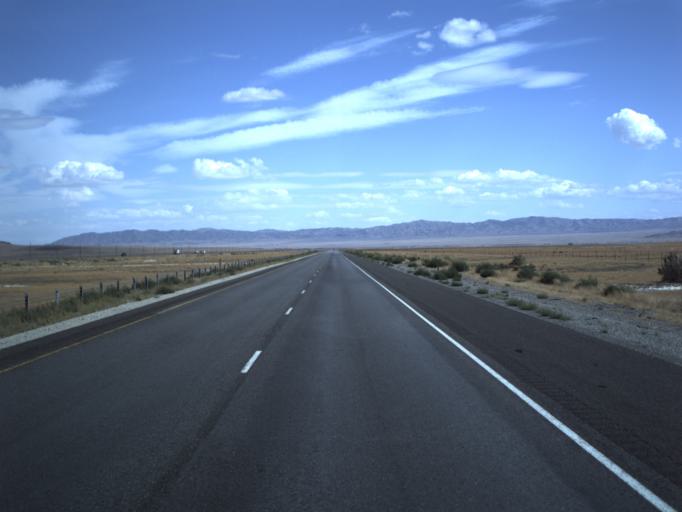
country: US
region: Utah
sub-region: Tooele County
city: Grantsville
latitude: 40.7258
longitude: -113.2053
